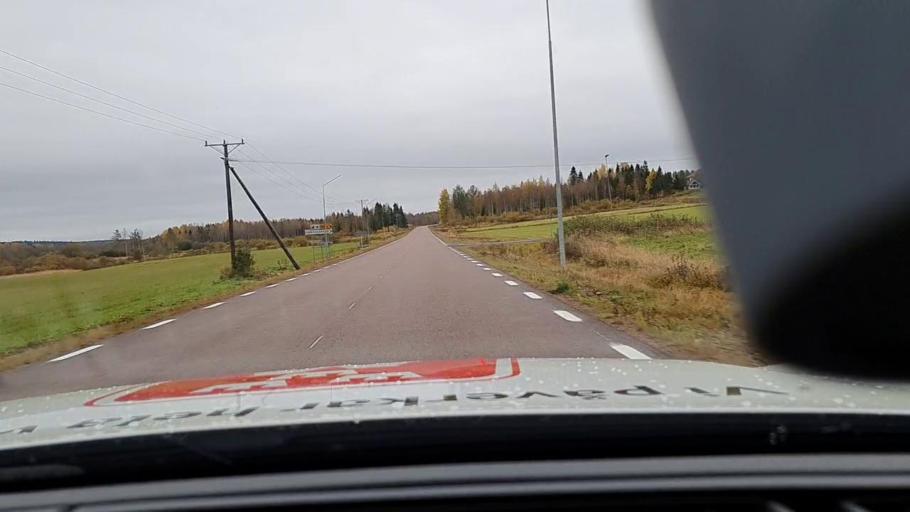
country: FI
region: Lapland
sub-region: Torniolaakso
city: Ylitornio
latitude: 66.1322
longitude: 23.9069
